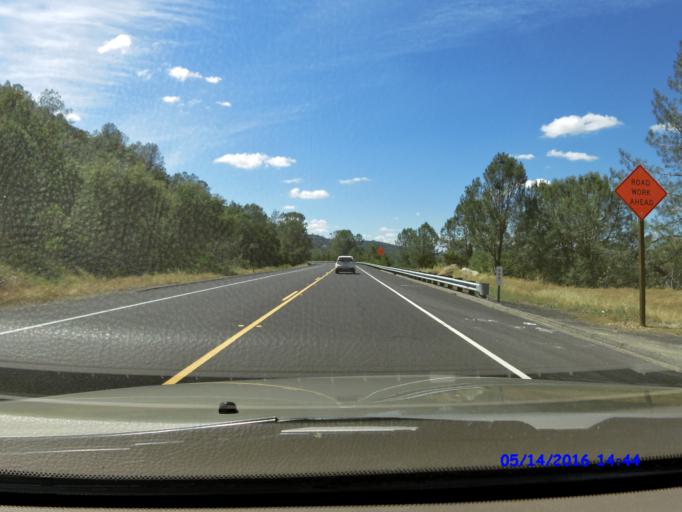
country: US
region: California
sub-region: Tuolumne County
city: Jamestown
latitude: 37.8387
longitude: -120.3660
